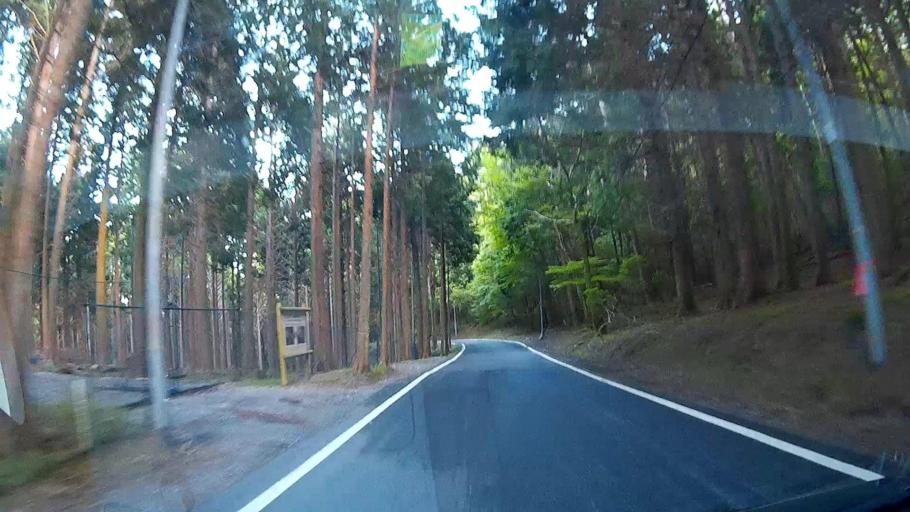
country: JP
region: Shizuoka
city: Shizuoka-shi
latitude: 35.1740
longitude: 138.2521
